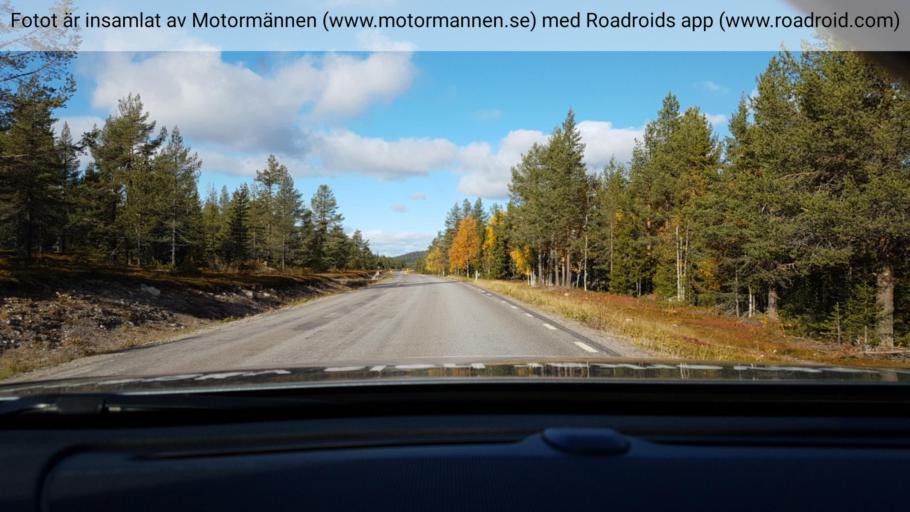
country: SE
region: Norrbotten
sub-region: Arjeplogs Kommun
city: Arjeplog
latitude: 65.9087
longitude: 18.3494
